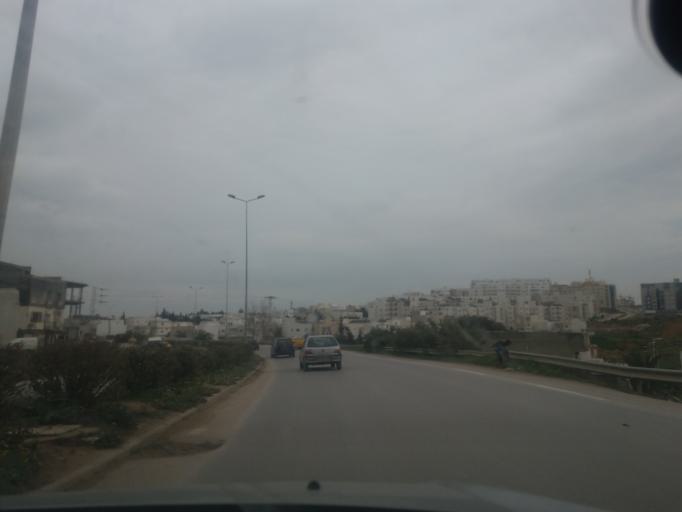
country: TN
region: Tunis
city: Tunis
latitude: 36.8536
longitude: 10.1356
